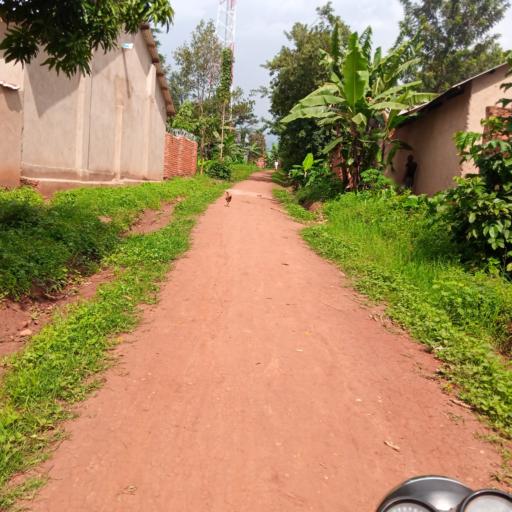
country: UG
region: Eastern Region
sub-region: Mbale District
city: Mbale
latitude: 1.1043
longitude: 34.1817
